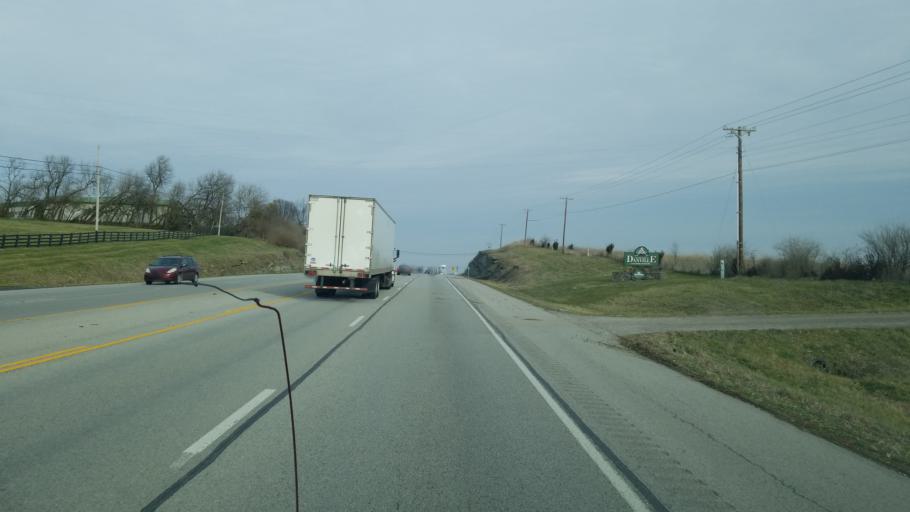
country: US
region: Kentucky
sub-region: Boyle County
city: Junction City
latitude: 37.6098
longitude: -84.7741
